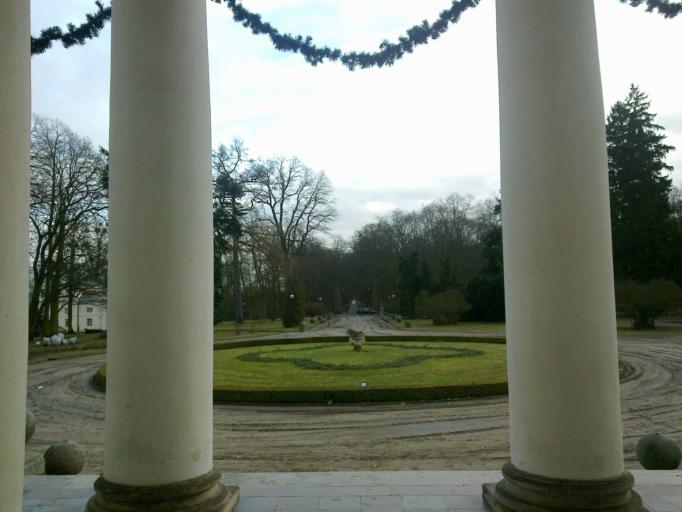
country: PL
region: Kujawsko-Pomorskie
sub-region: Powiat zninski
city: Labiszyn
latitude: 52.9068
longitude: 17.8817
